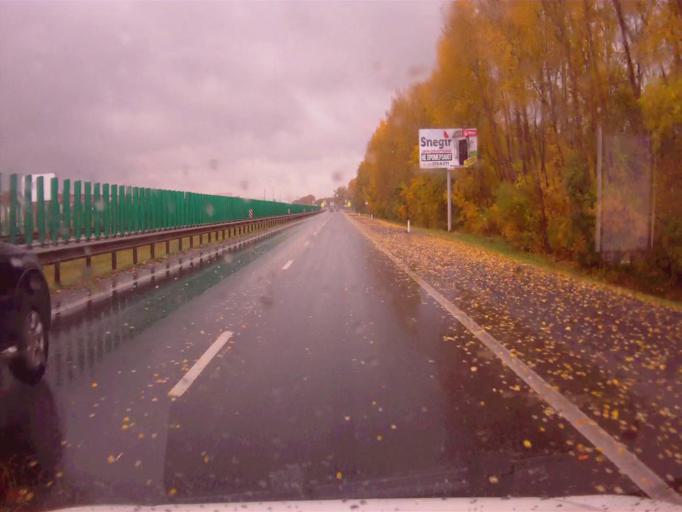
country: RU
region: Chelyabinsk
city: Dolgoderevenskoye
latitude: 55.2798
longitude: 61.3434
